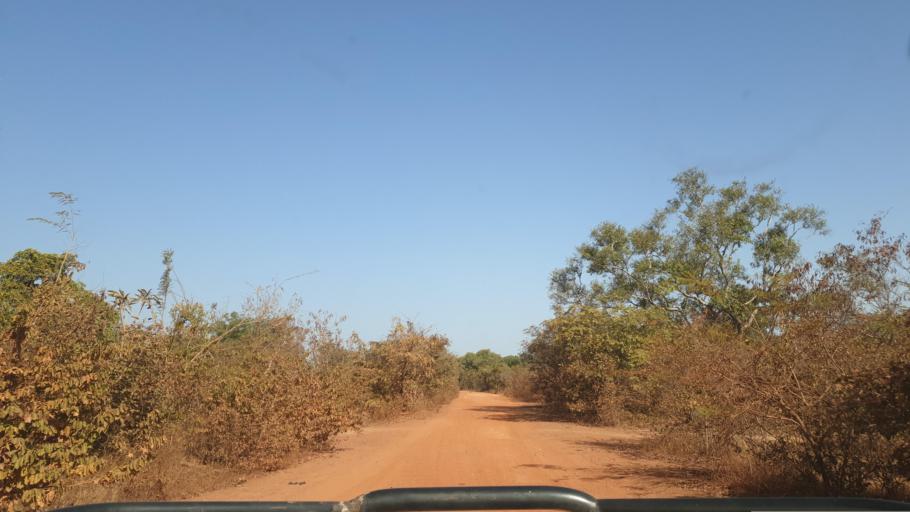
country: ML
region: Sikasso
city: Bougouni
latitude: 11.7819
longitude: -6.9083
